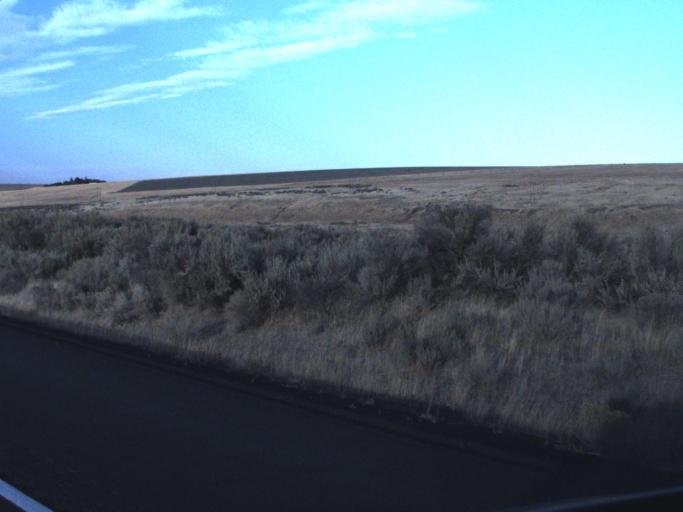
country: US
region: Washington
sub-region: Adams County
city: Ritzville
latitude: 47.0045
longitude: -118.5283
